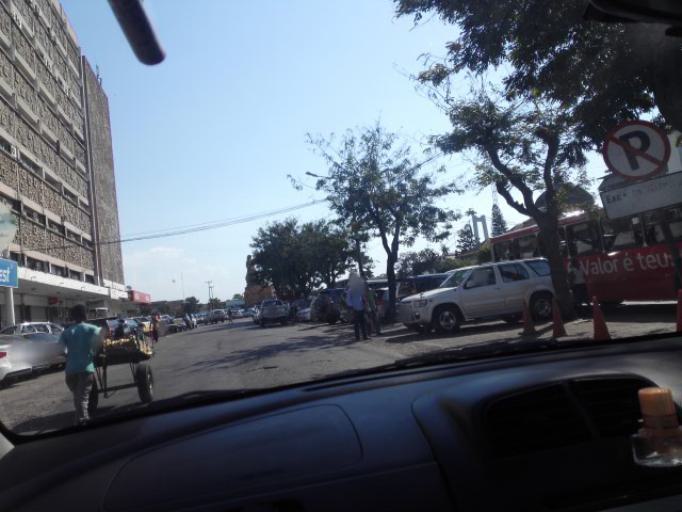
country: MZ
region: Maputo City
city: Maputo
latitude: -25.9705
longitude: 32.5662
